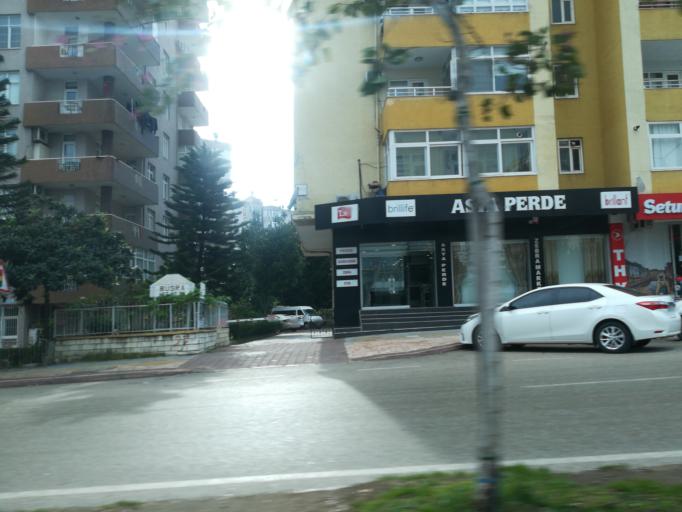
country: TR
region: Adana
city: Adana
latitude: 37.0404
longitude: 35.3022
